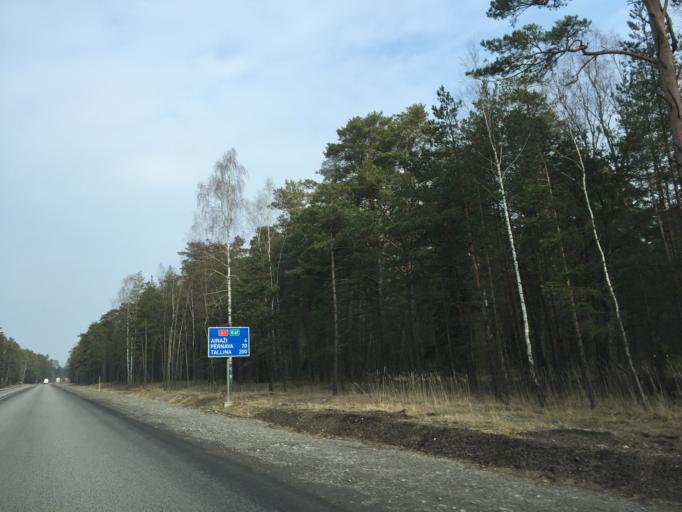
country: LV
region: Salacgrivas
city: Ainazi
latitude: 57.8222
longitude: 24.3463
